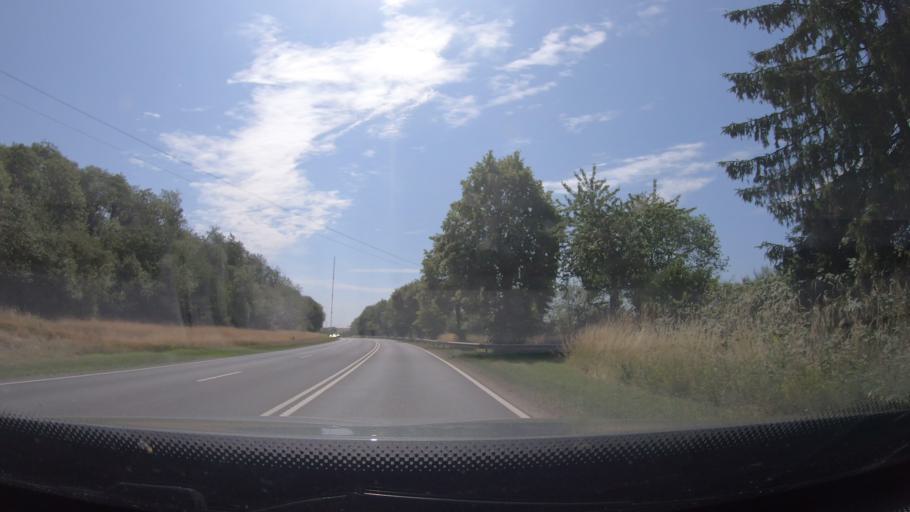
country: LU
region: Diekirch
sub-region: Canton de Clervaux
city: Hosingen
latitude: 50.0307
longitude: 6.0823
